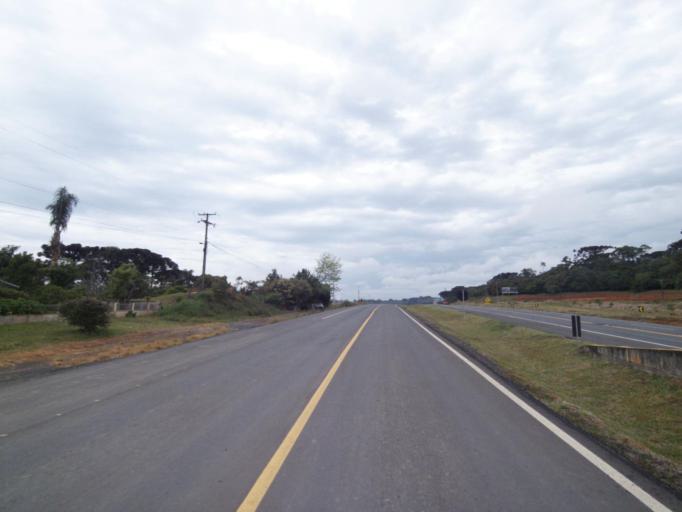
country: BR
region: Parana
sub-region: Irati
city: Irati
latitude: -25.4543
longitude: -50.6137
